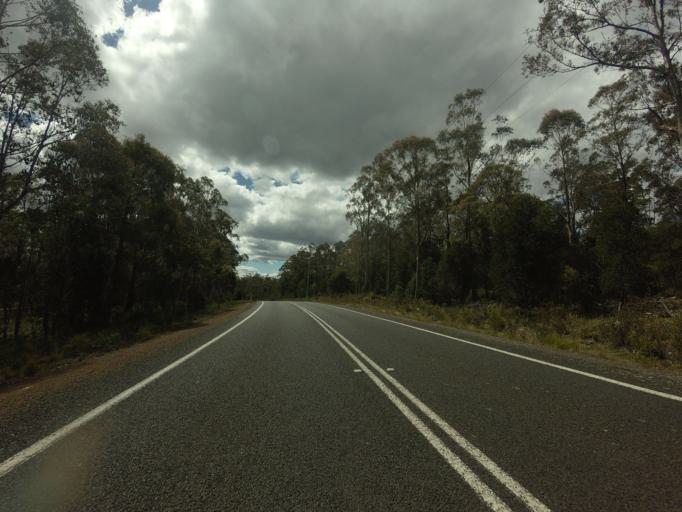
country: AU
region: Tasmania
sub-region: Northern Midlands
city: Evandale
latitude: -42.0065
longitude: 147.7236
